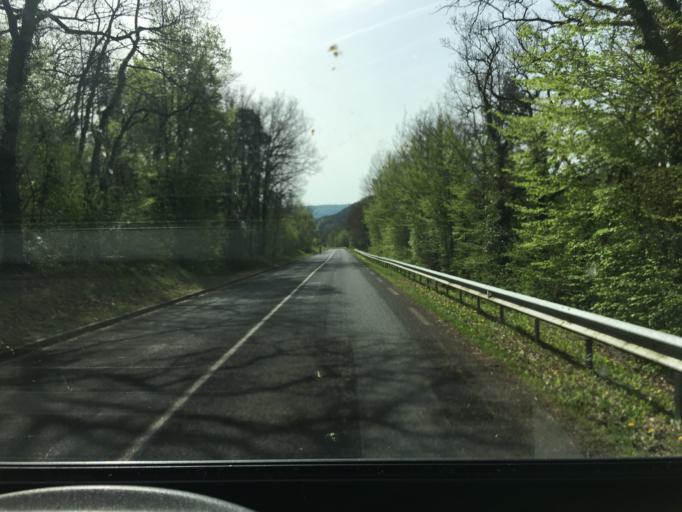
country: FR
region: Lorraine
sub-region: Departement de Meurthe-et-Moselle
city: Velaine-en-Haye
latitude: 48.6619
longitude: 6.0258
